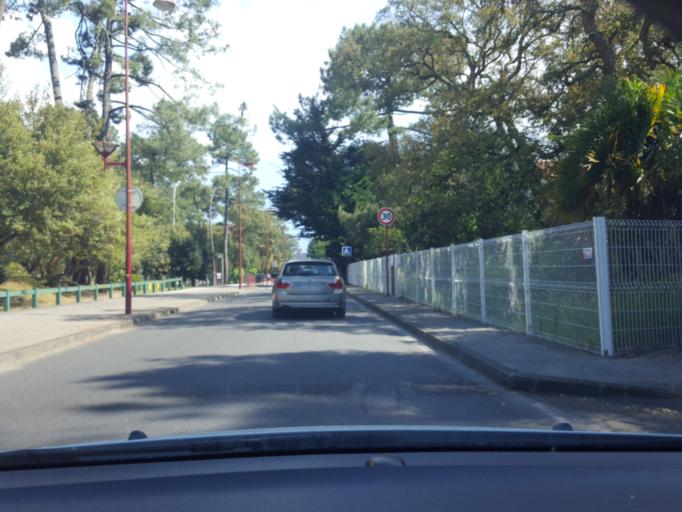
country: FR
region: Aquitaine
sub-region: Departement des Landes
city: Tarnos
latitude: 43.5519
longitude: -1.4918
